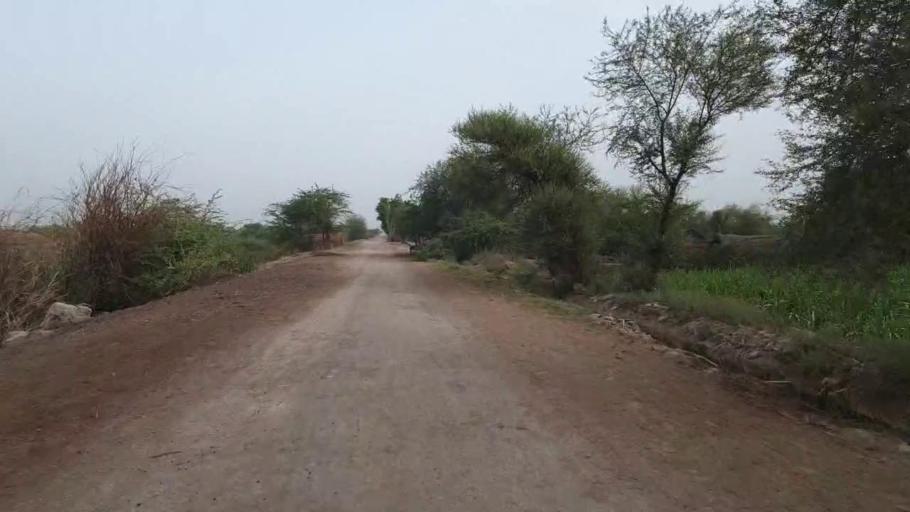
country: PK
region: Sindh
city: Daur
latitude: 26.4256
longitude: 68.2251
